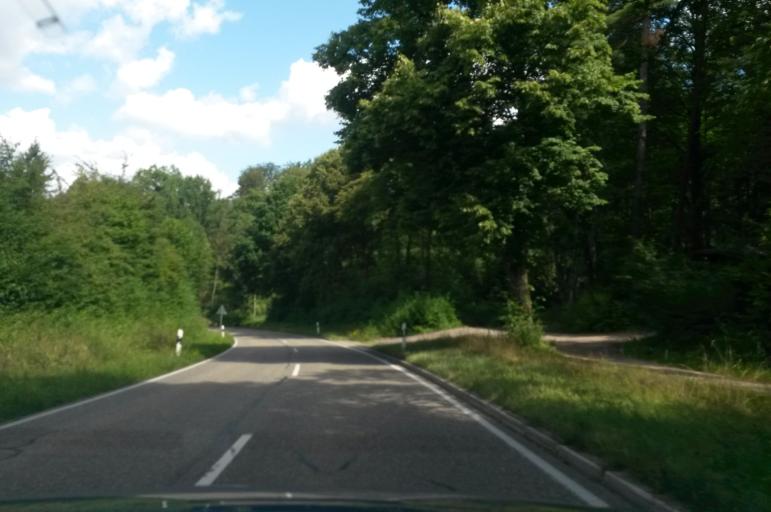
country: DE
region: Baden-Wuerttemberg
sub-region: Karlsruhe Region
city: Bad Herrenalb
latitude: 48.8755
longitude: 8.4562
